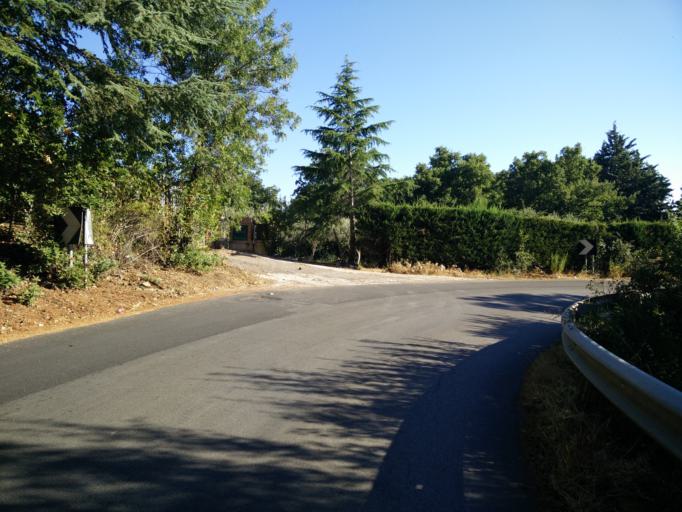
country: IT
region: Sicily
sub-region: Palermo
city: Castelbuono
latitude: 37.9226
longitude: 14.0857
